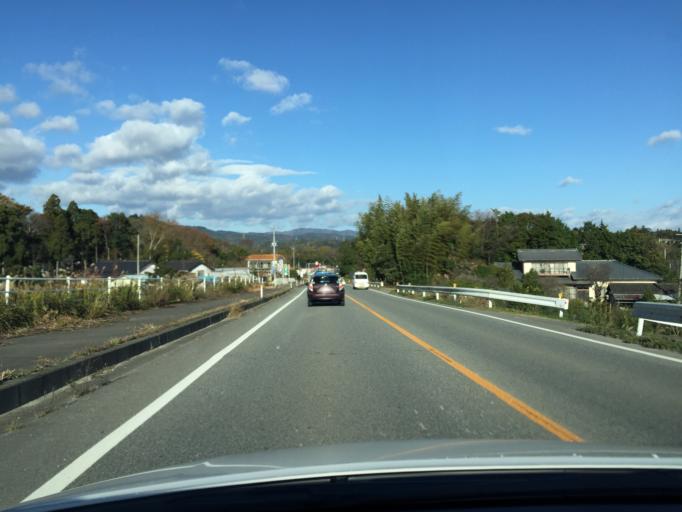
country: JP
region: Fukushima
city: Iwaki
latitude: 37.1974
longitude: 140.9970
